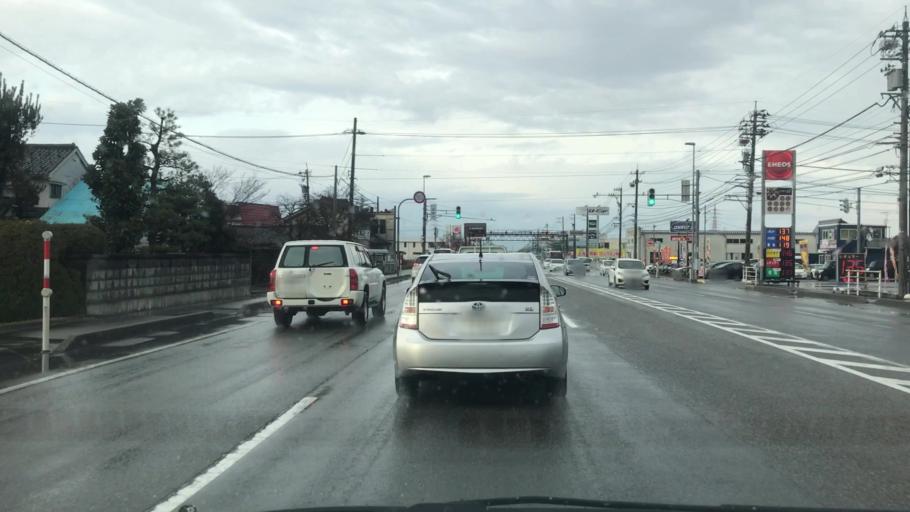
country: JP
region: Toyama
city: Toyama-shi
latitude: 36.6443
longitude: 137.2095
